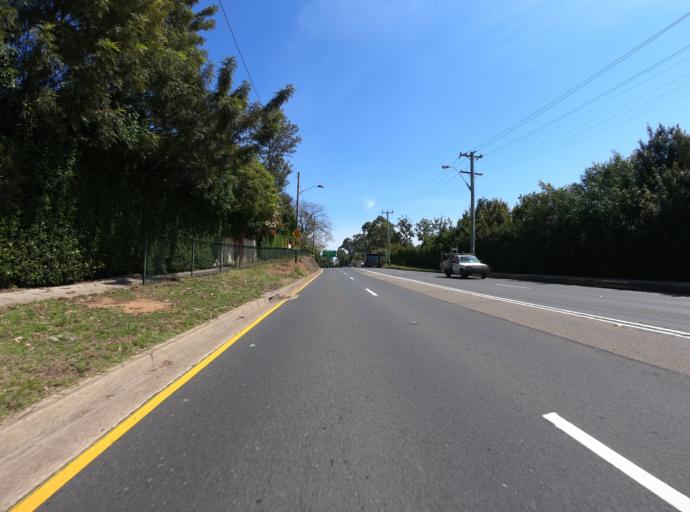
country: AU
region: New South Wales
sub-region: The Hills Shire
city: Castle Hill
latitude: -33.7322
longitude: 151.0230
